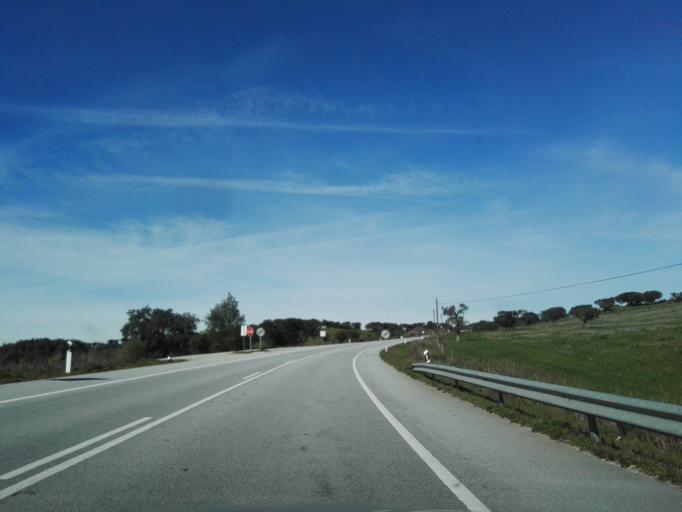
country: PT
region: Portalegre
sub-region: Portalegre
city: Urra
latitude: 39.1971
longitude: -7.3640
